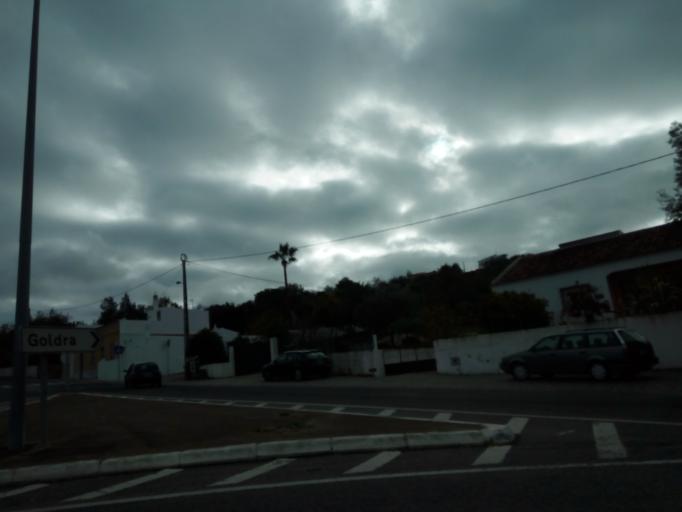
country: PT
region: Faro
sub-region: Loule
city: Loule
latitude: 37.1299
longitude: -8.0045
